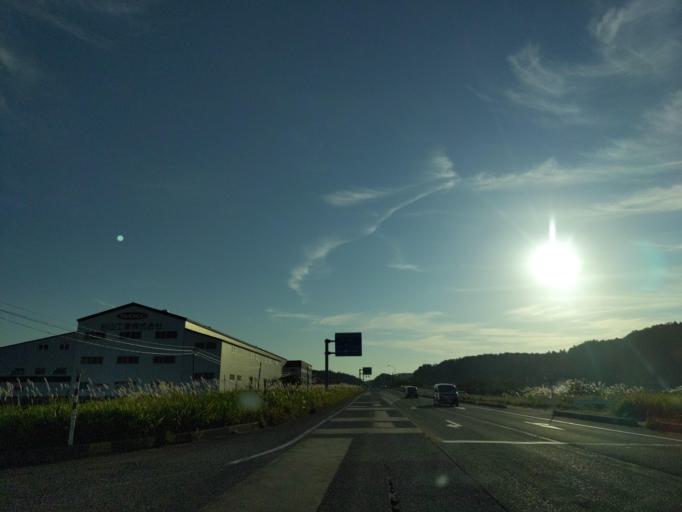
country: JP
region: Niigata
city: Nagaoka
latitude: 37.5729
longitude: 138.7453
